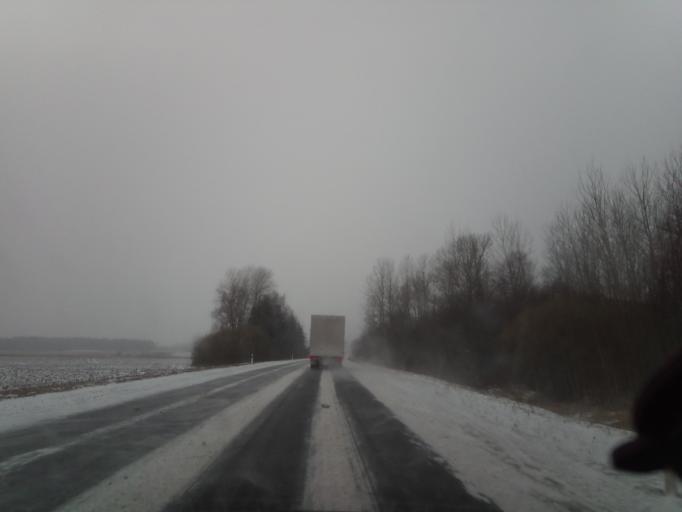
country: LT
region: Utenos apskritis
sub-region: Anyksciai
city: Anyksciai
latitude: 55.3654
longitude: 25.0008
